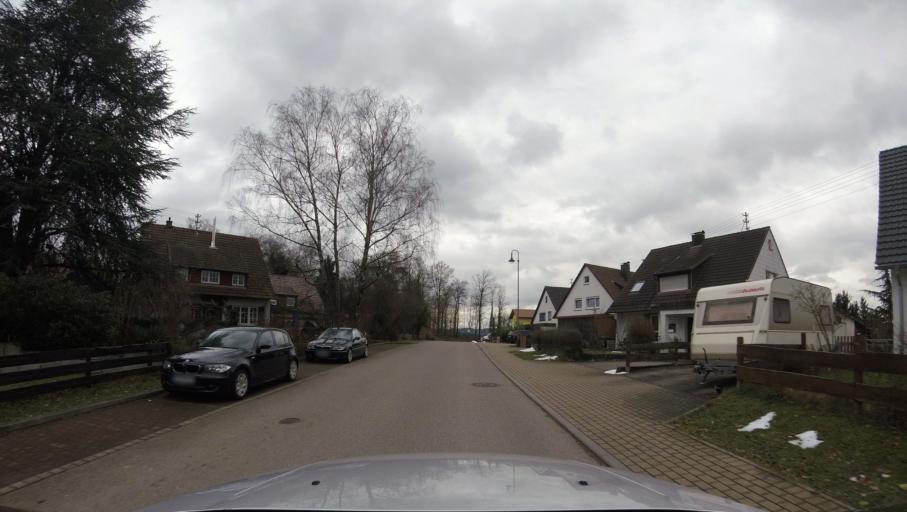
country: DE
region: Baden-Wuerttemberg
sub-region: Regierungsbezirk Stuttgart
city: Oppenweiler
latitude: 48.9734
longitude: 9.4442
